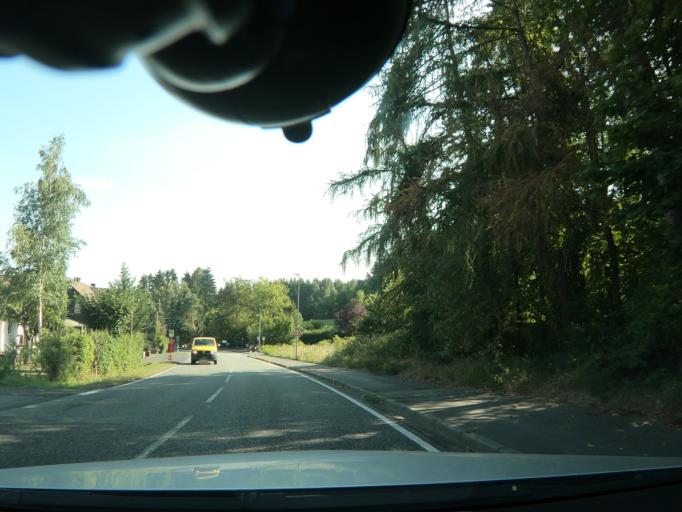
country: DE
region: Hesse
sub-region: Regierungsbezirk Giessen
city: Marburg an der Lahn
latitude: 50.7918
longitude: 8.8173
